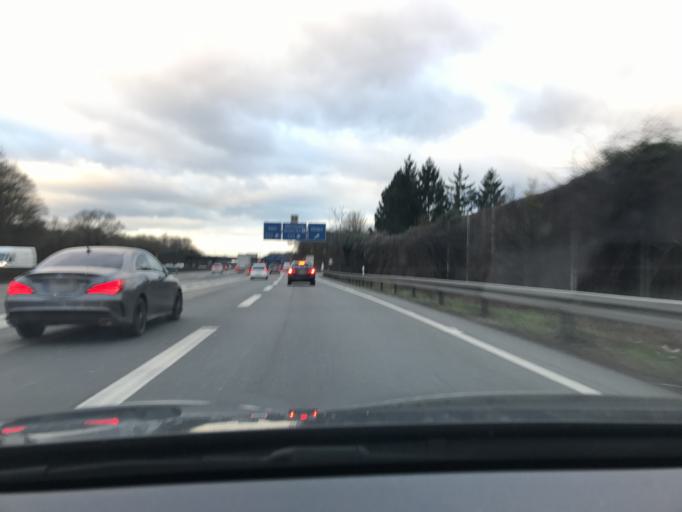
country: DE
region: North Rhine-Westphalia
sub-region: Regierungsbezirk Dusseldorf
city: Hilden
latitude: 51.1968
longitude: 6.9489
